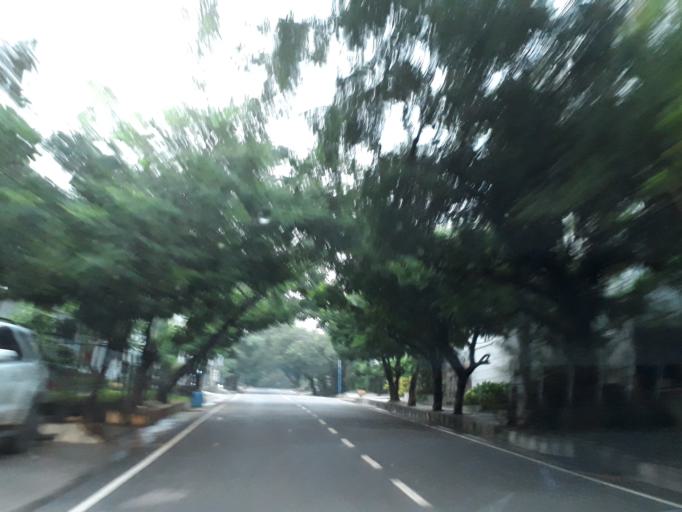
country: IN
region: Telangana
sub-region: Rangareddi
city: Kukatpalli
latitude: 17.4357
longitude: 78.4054
